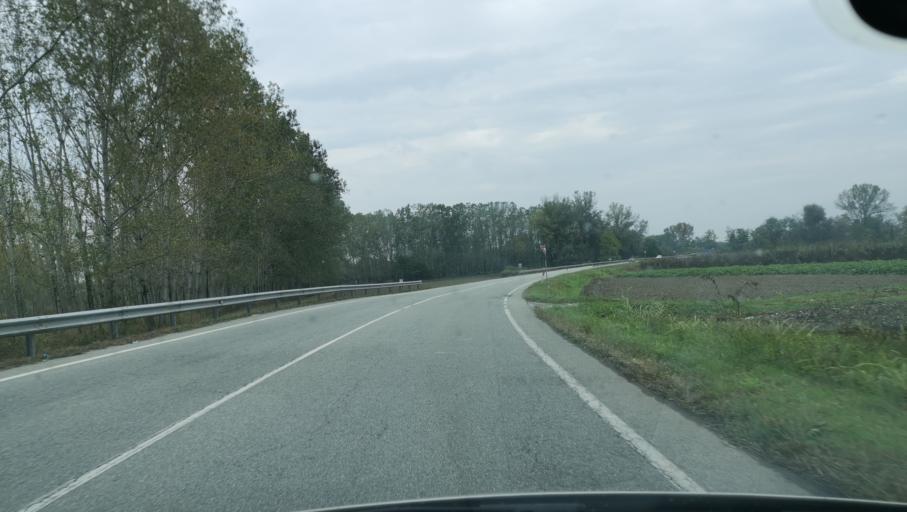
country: IT
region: Piedmont
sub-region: Provincia di Torino
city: Castiglione Torinese
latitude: 45.1265
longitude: 7.7867
